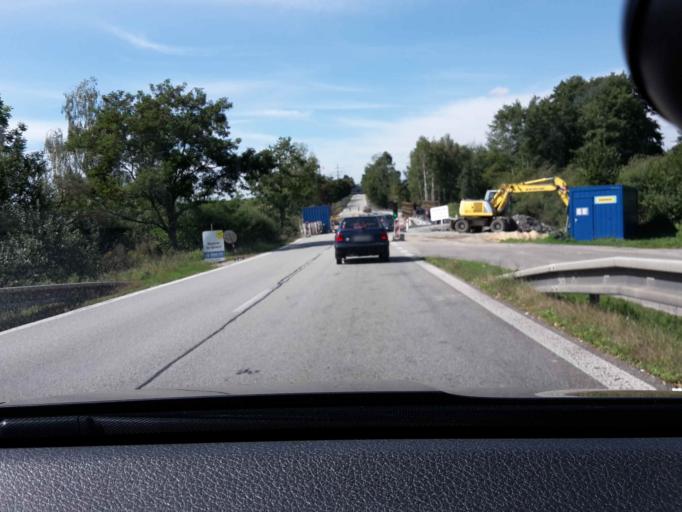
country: CZ
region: Jihocesky
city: Kardasova Recice
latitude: 49.1752
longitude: 14.8799
